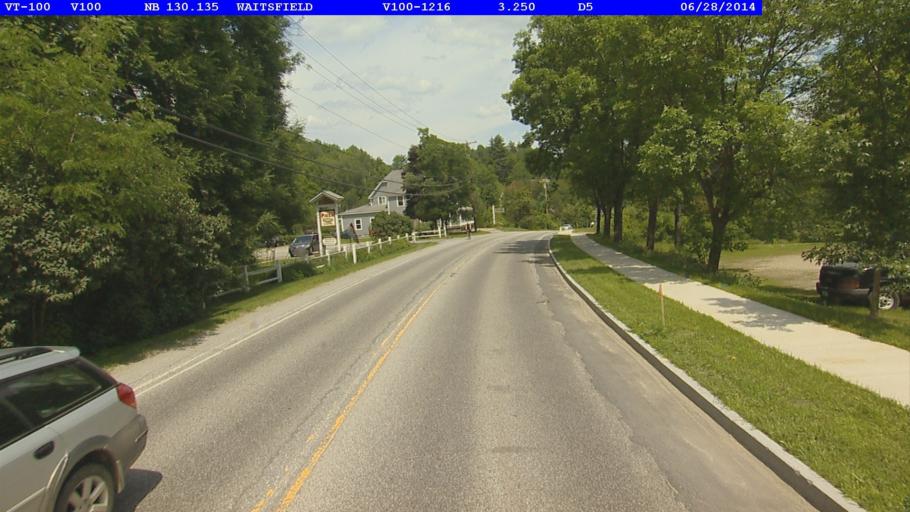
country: US
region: Vermont
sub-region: Washington County
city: Waterbury
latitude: 44.1879
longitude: -72.8316
